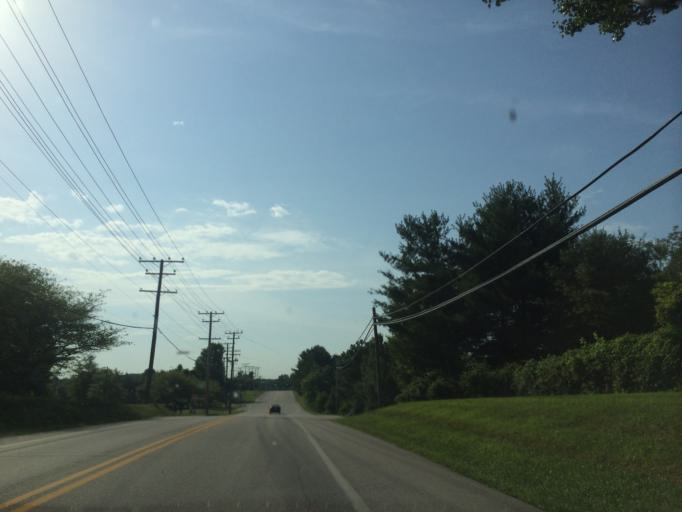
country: US
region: Maryland
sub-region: Howard County
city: Highland
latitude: 39.1905
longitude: -76.9276
